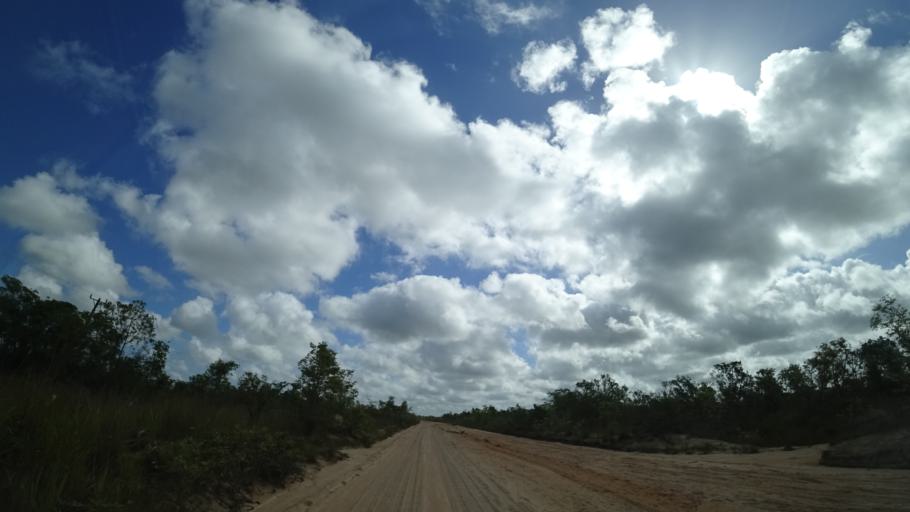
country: MZ
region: Sofala
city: Dondo
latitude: -19.4579
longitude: 34.7188
